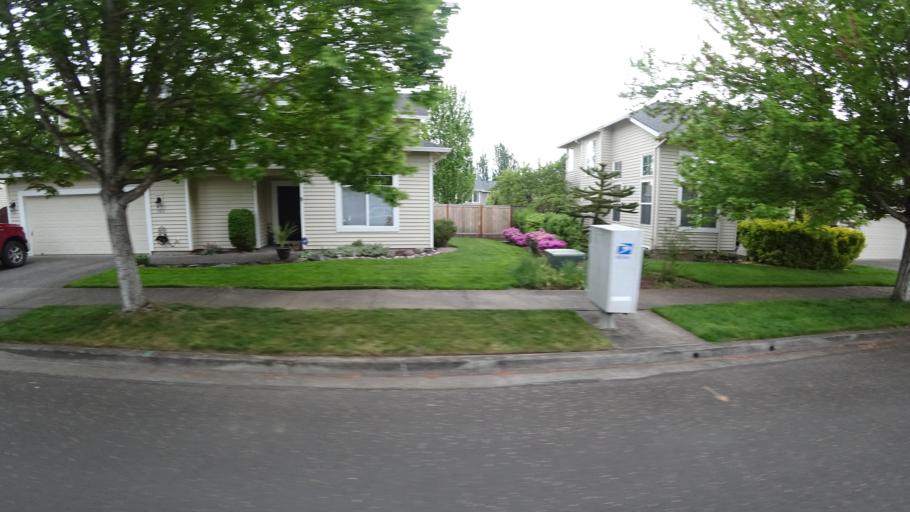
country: US
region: Oregon
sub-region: Washington County
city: Hillsboro
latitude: 45.5450
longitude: -122.9731
